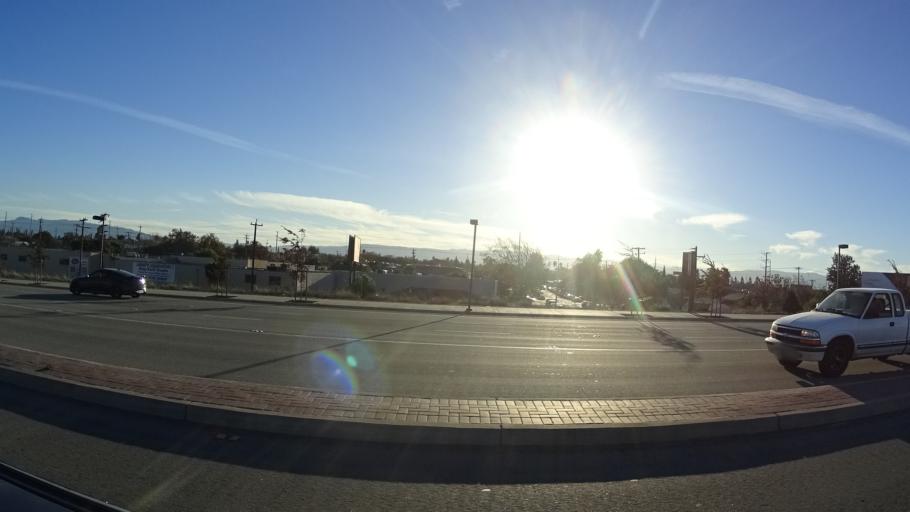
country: US
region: California
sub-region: Santa Clara County
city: San Jose
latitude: 37.3482
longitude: -121.9173
